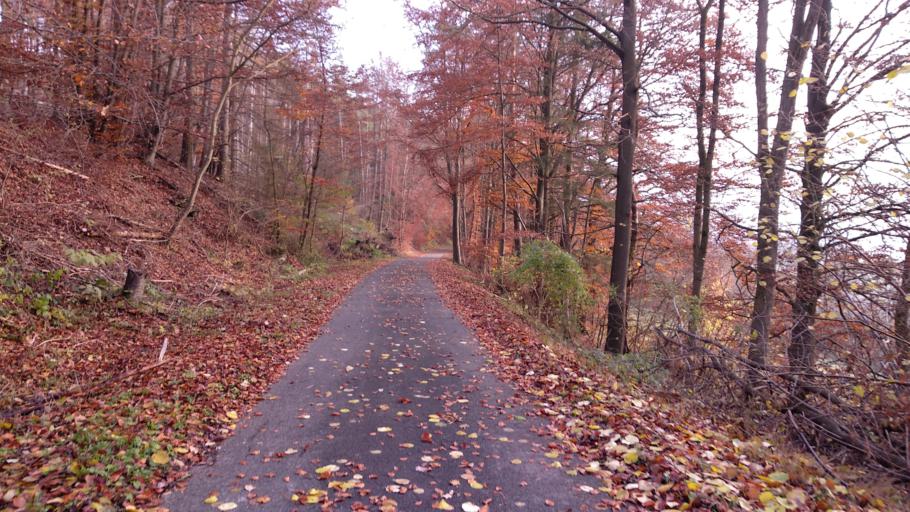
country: DE
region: North Rhine-Westphalia
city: Beverungen
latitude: 51.6687
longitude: 9.3442
